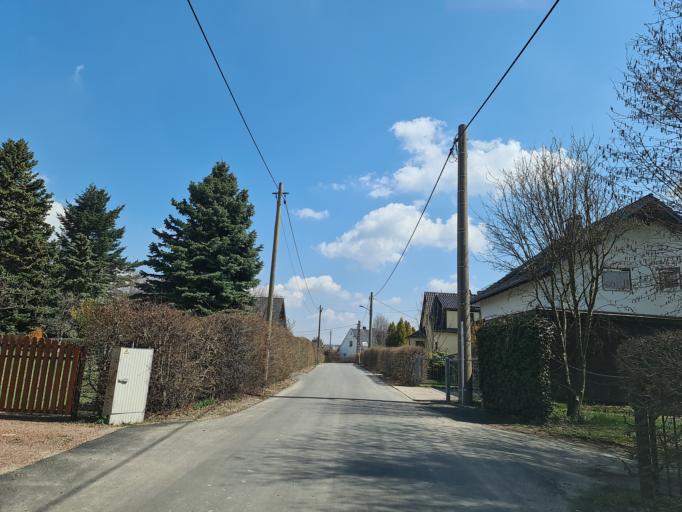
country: DE
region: Saxony
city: Oelsnitz
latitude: 50.7081
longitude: 12.7255
